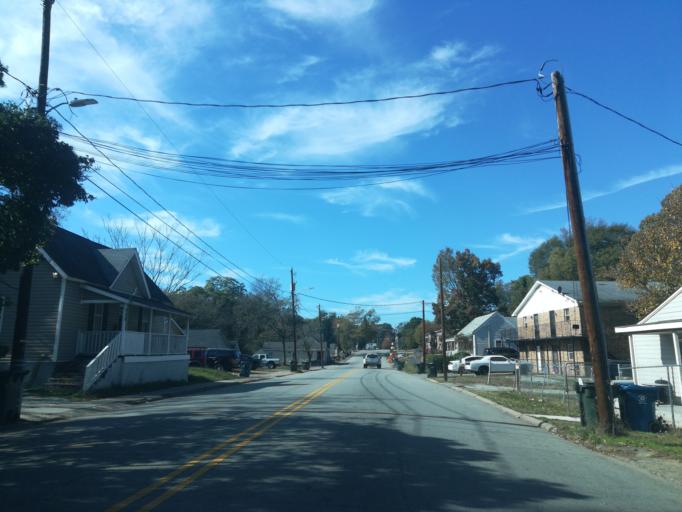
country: US
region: North Carolina
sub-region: Durham County
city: Durham
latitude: 35.9929
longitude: -78.8881
